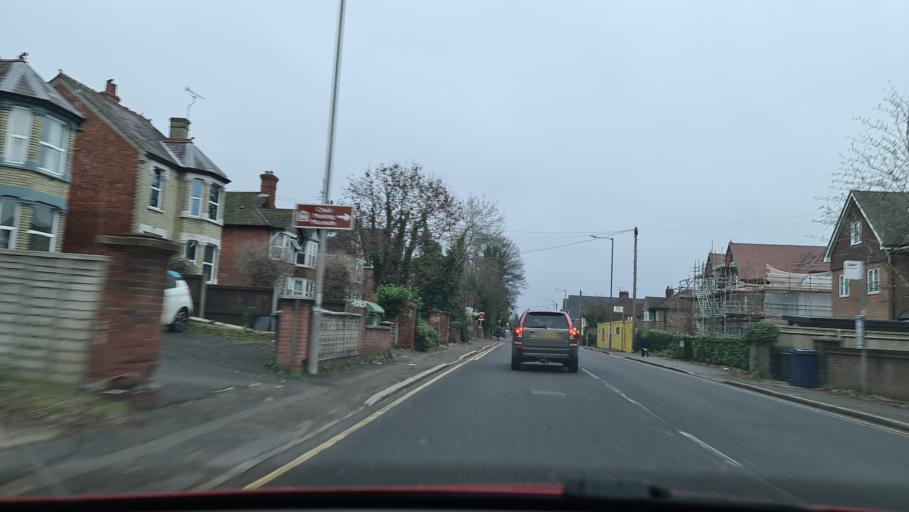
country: GB
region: England
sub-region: Buckinghamshire
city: High Wycombe
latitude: 51.6375
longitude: -0.7727
